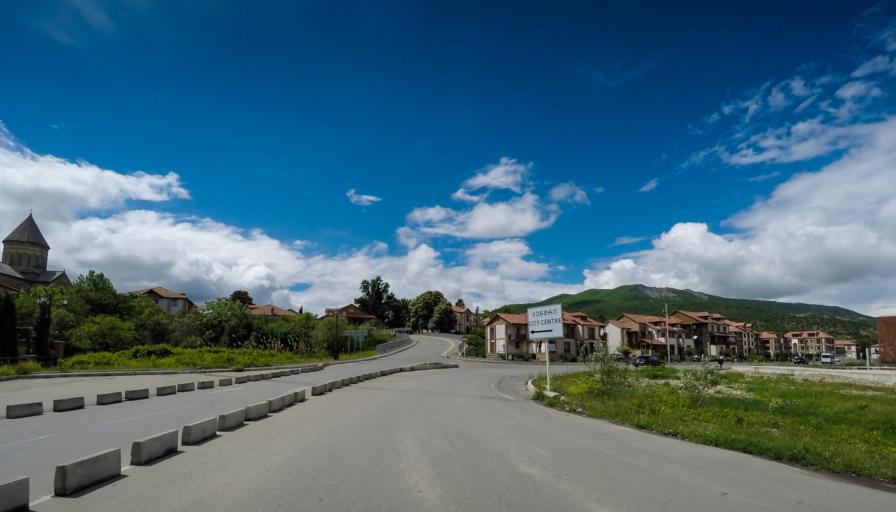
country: GE
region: Mtskheta-Mtianeti
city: Mtskheta
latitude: 41.8431
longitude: 44.7231
